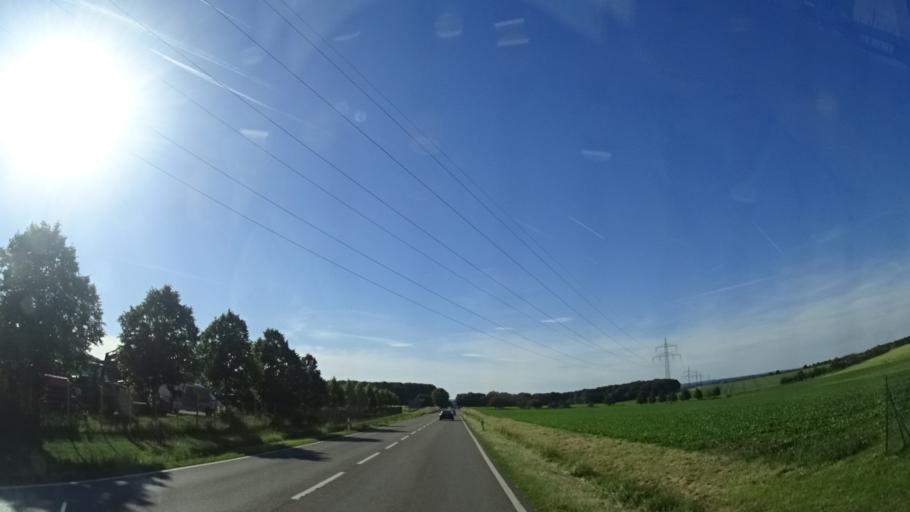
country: DE
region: Baden-Wuerttemberg
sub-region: Regierungsbezirk Stuttgart
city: Untermunkheim
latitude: 49.1786
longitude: 9.7083
